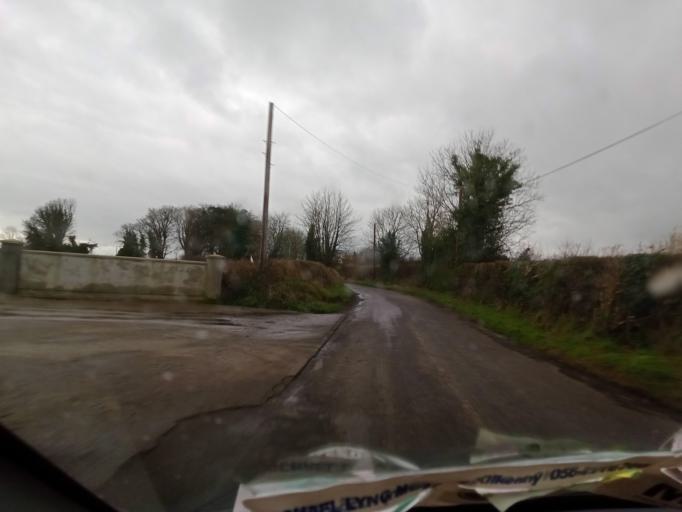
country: IE
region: Munster
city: Fethard
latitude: 52.5220
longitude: -7.7567
